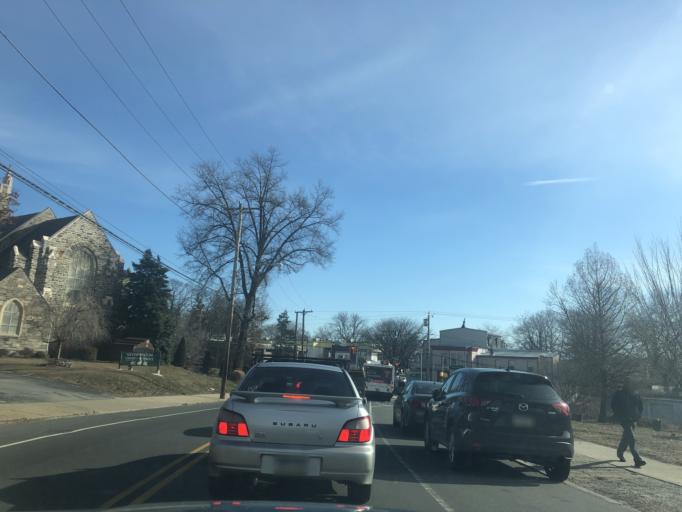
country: US
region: Pennsylvania
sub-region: Montgomery County
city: Bala-Cynwyd
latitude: 40.0370
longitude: -75.2197
